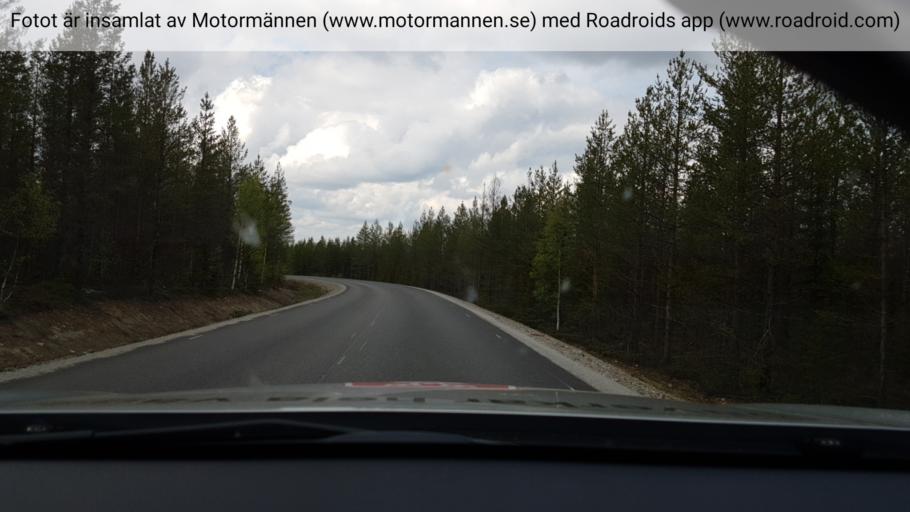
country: SE
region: Vaesterbotten
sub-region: Lycksele Kommun
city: Lycksele
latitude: 64.0553
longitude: 18.4197
